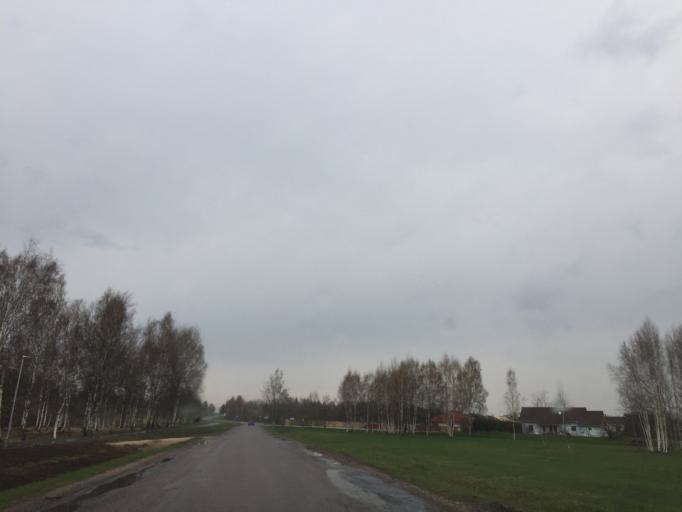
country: EE
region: Tartu
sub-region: UElenurme vald
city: Ulenurme
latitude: 58.3037
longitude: 26.7242
